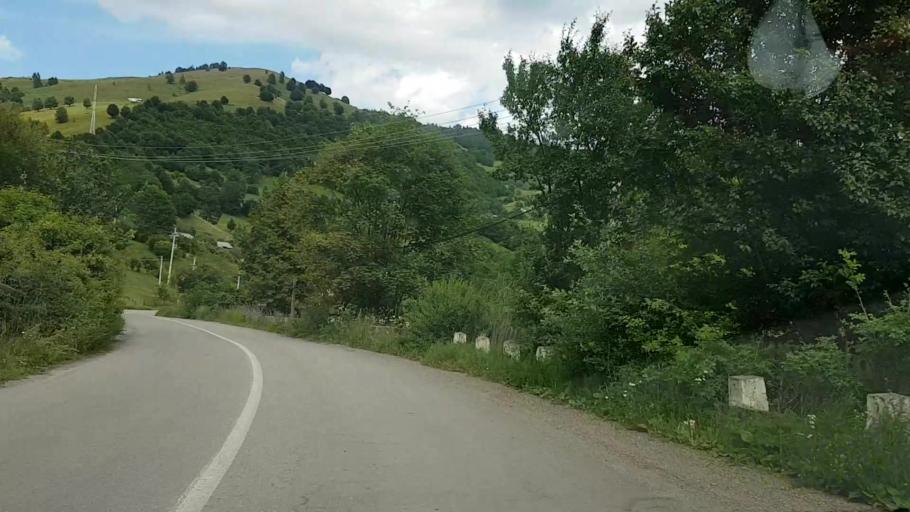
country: RO
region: Neamt
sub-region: Comuna Hangu
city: Hangu
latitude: 47.0363
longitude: 26.0614
